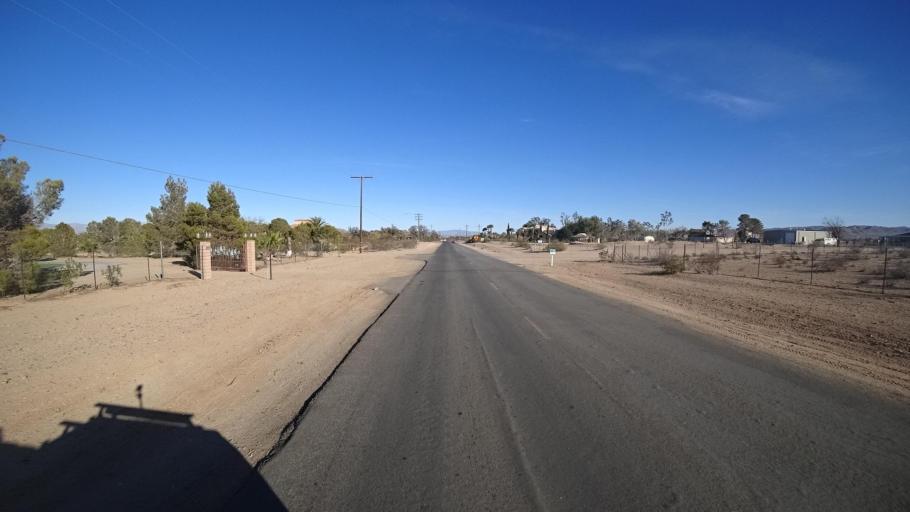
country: US
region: California
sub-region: Kern County
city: Ridgecrest
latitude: 35.6299
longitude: -117.7082
